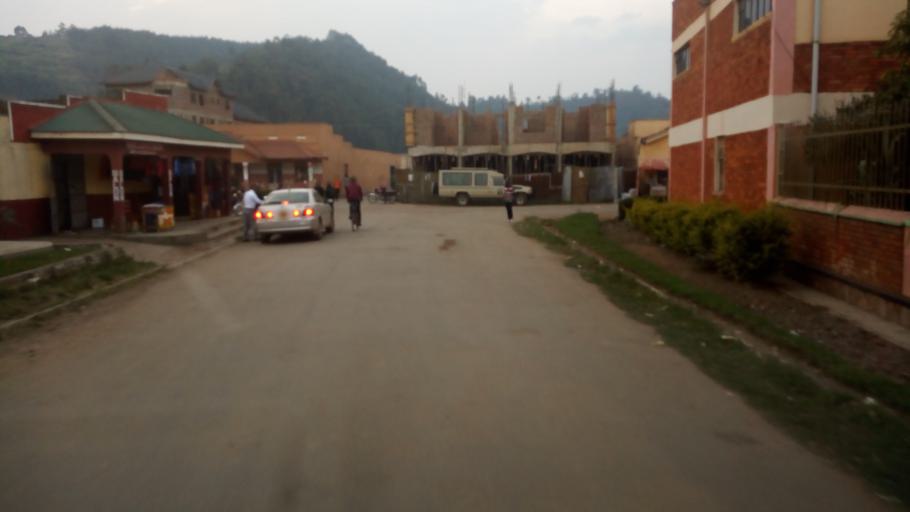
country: UG
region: Western Region
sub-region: Kisoro District
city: Kisoro
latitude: -1.2813
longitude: 29.6918
